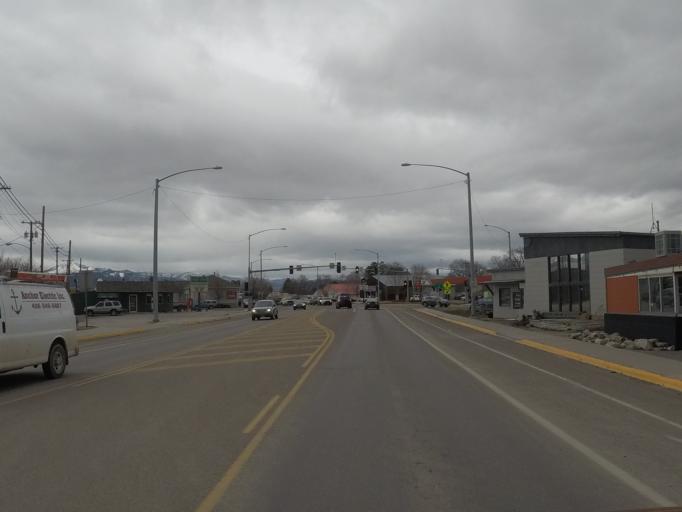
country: US
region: Montana
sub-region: Missoula County
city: Missoula
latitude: 46.8776
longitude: -114.0121
